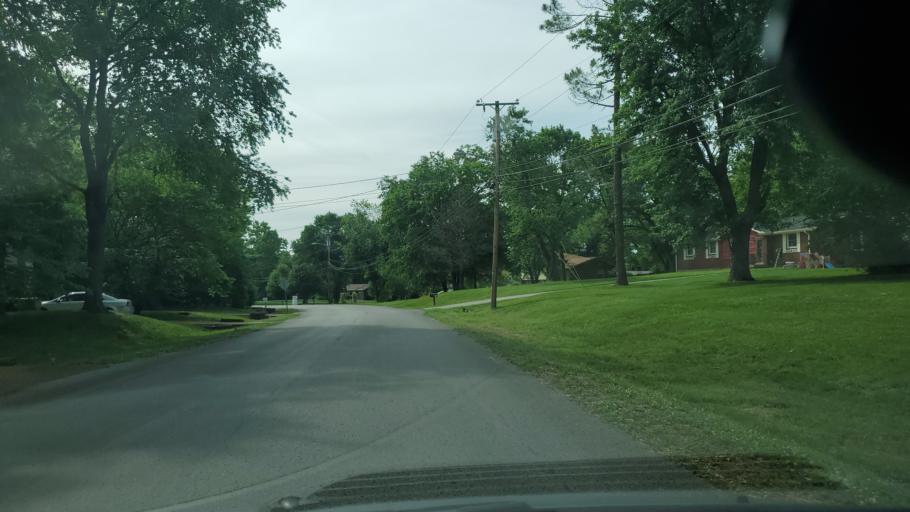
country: US
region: Tennessee
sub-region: Davidson County
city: Lakewood
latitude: 36.2080
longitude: -86.6854
